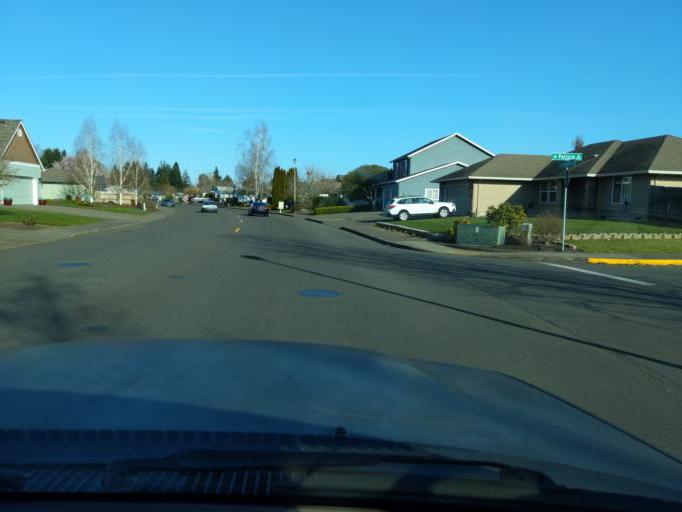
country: US
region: Oregon
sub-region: Yamhill County
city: McMinnville
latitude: 45.2018
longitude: -123.2158
